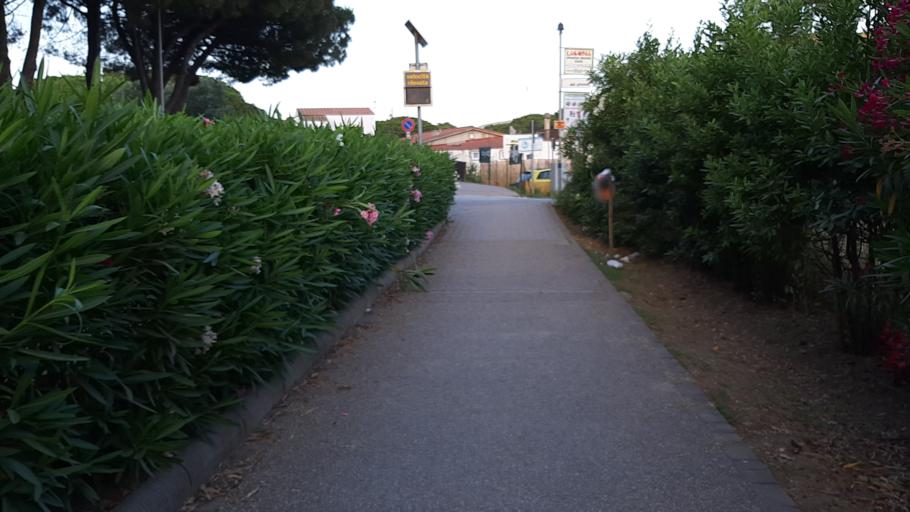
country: IT
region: Tuscany
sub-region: Provincia di Livorno
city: Portoferraio
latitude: 42.7608
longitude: 10.3113
